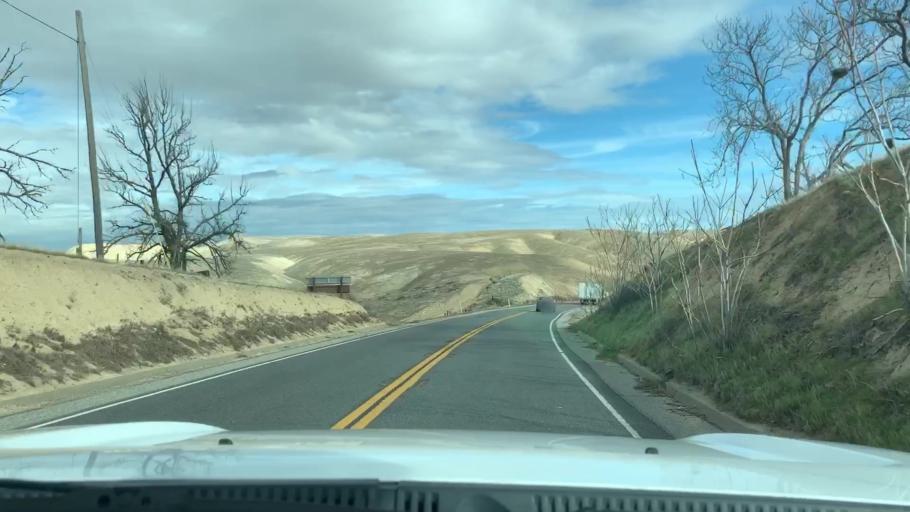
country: US
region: California
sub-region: Kern County
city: Maricopa
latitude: 34.9637
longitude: -119.4458
